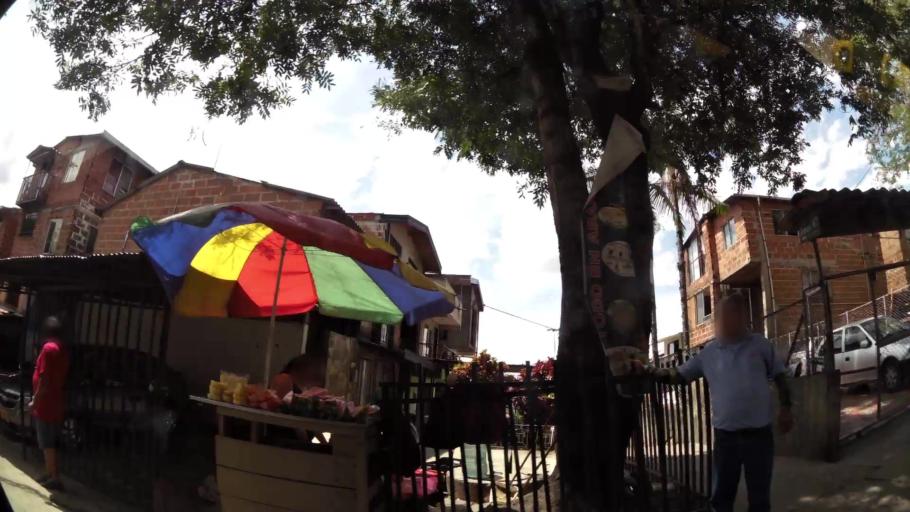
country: CO
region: Antioquia
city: Bello
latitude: 6.3463
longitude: -75.5538
